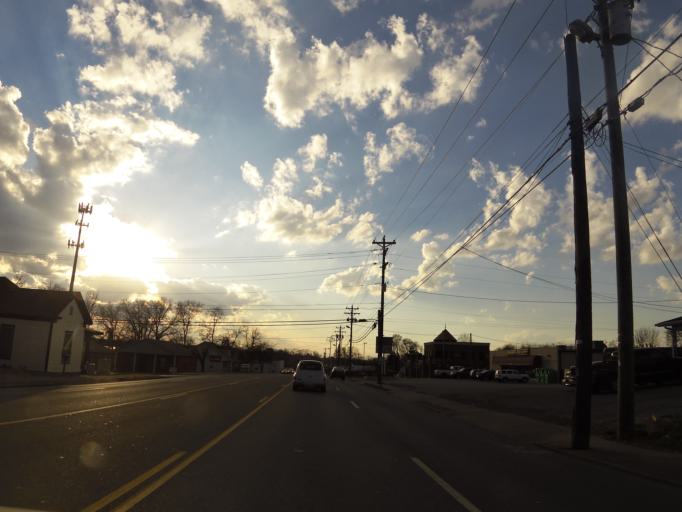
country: US
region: Tennessee
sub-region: Wilson County
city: Lebanon
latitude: 36.2125
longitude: -86.2913
